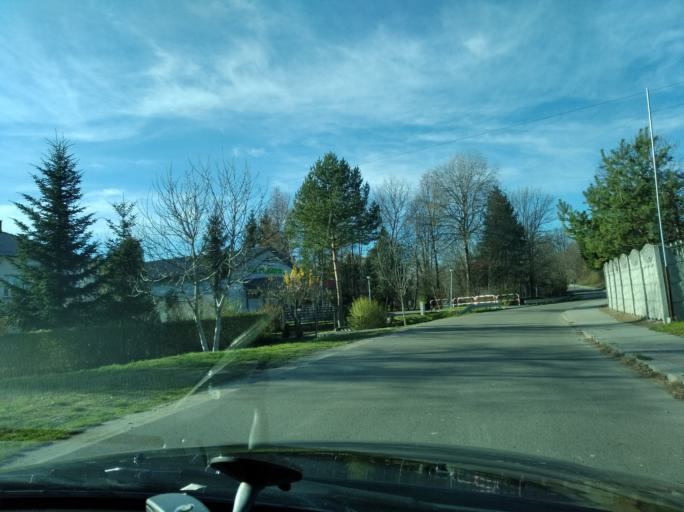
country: PL
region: Subcarpathian Voivodeship
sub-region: Powiat rzeszowski
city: Lutoryz
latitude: 49.9670
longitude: 21.9090
